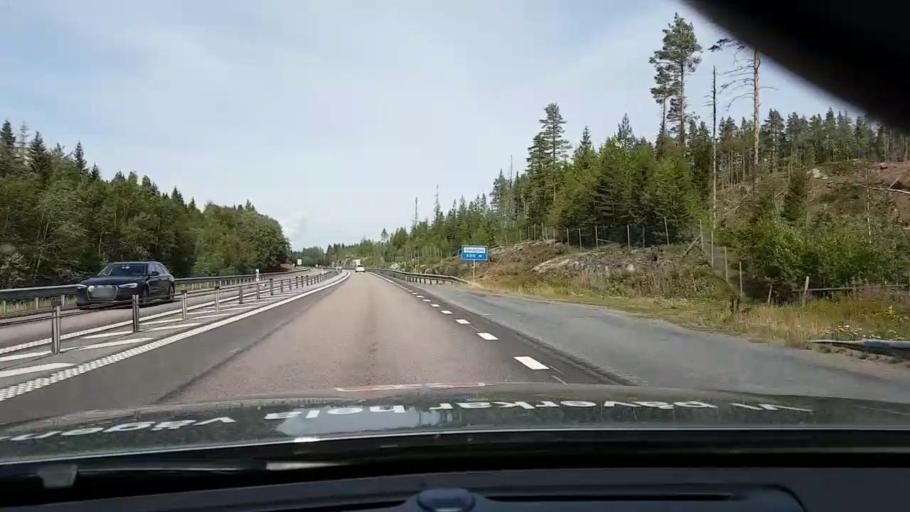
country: SE
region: Vaesternorrland
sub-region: OErnskoeldsviks Kommun
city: Husum
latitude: 63.4312
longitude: 19.2095
